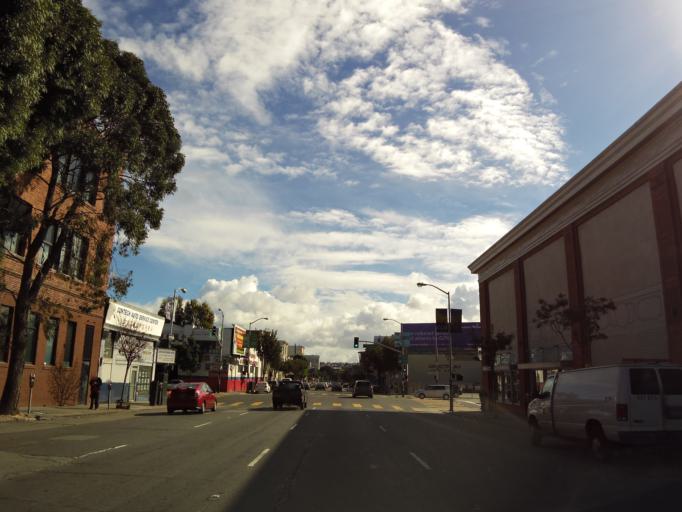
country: US
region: California
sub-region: San Francisco County
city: San Francisco
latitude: 37.7732
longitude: -122.4133
